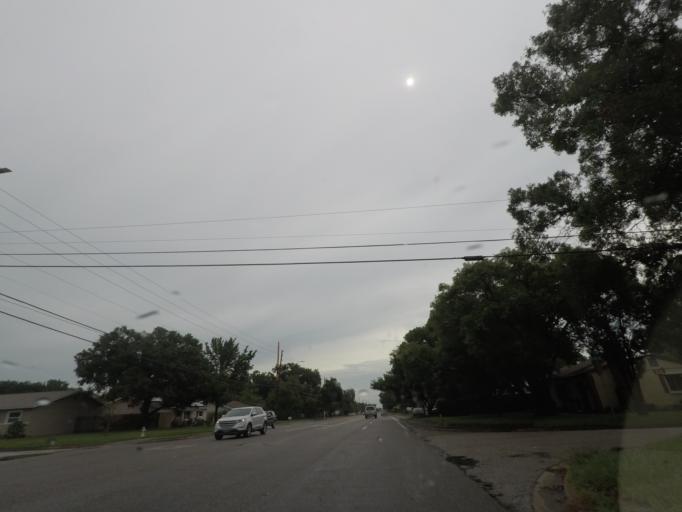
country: US
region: Florida
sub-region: Pinellas County
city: West and East Lealman
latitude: 27.8064
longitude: -82.6900
